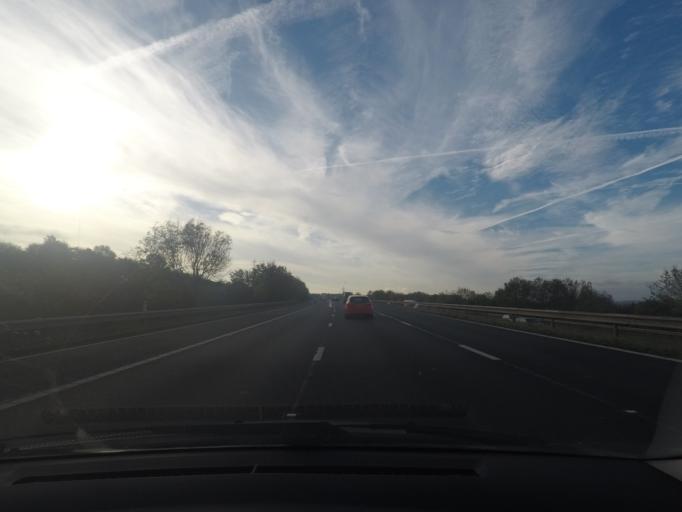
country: GB
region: England
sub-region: Barnsley
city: Darton
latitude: 53.5716
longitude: -1.5411
